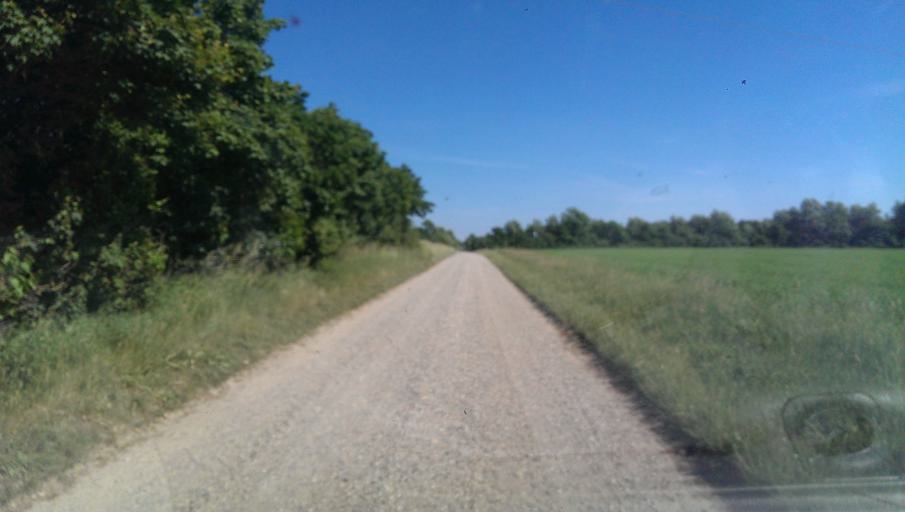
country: DK
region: South Denmark
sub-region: Fano Kommune
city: Nordby
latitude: 55.5295
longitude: 8.3855
